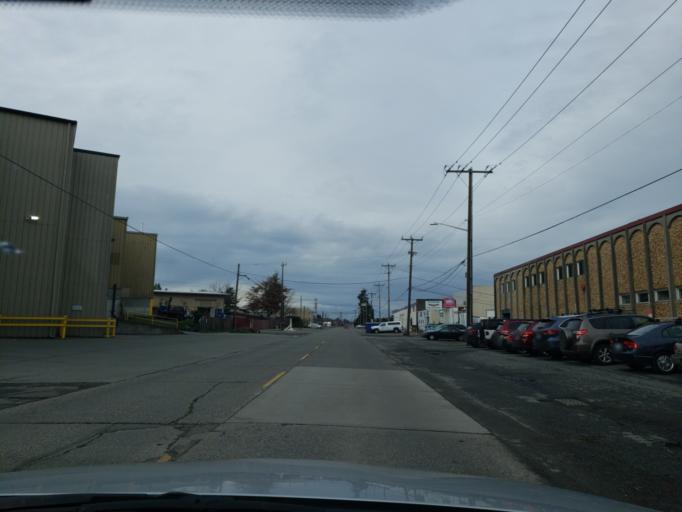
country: US
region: Washington
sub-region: King County
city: Seattle
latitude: 47.6609
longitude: -122.3874
